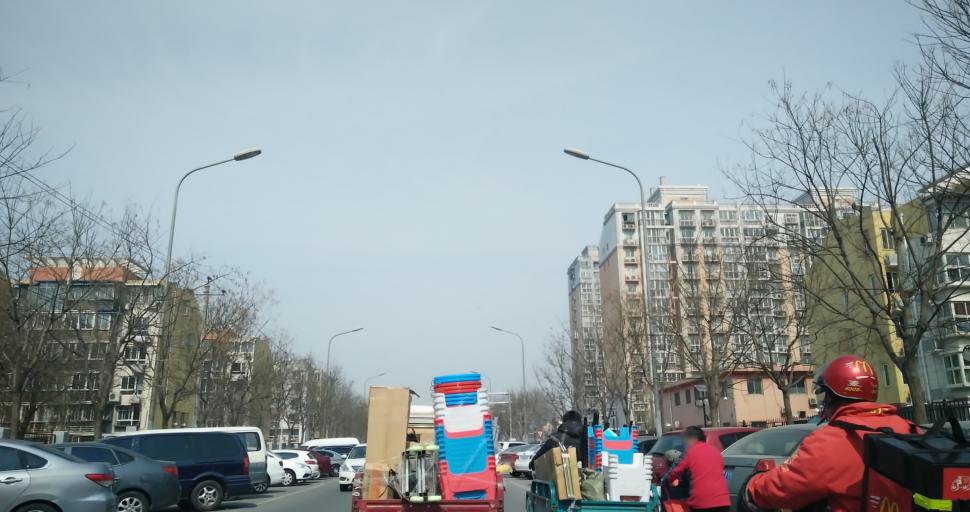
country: CN
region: Beijing
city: Jiugong
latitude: 39.8576
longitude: 116.5041
